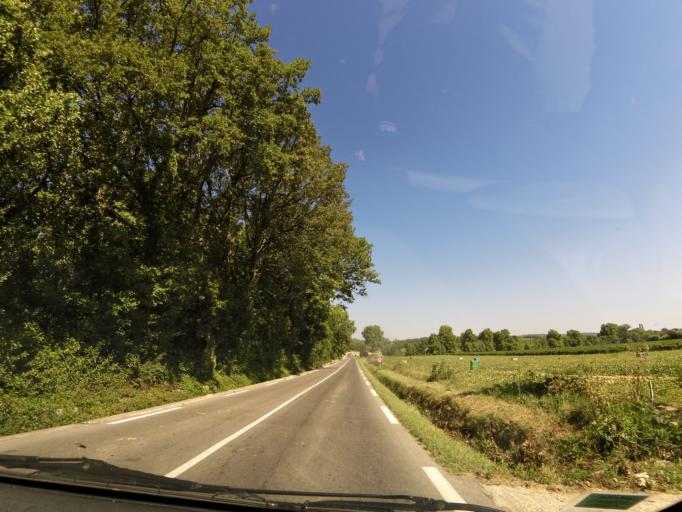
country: FR
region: Languedoc-Roussillon
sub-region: Departement du Gard
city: Villevieille
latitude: 43.8090
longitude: 4.0942
